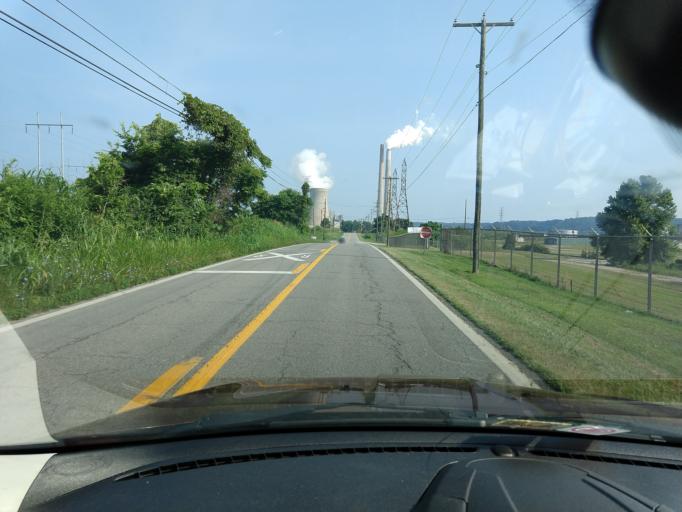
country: US
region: West Virginia
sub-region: Mason County
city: New Haven
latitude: 38.9634
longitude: -81.9269
